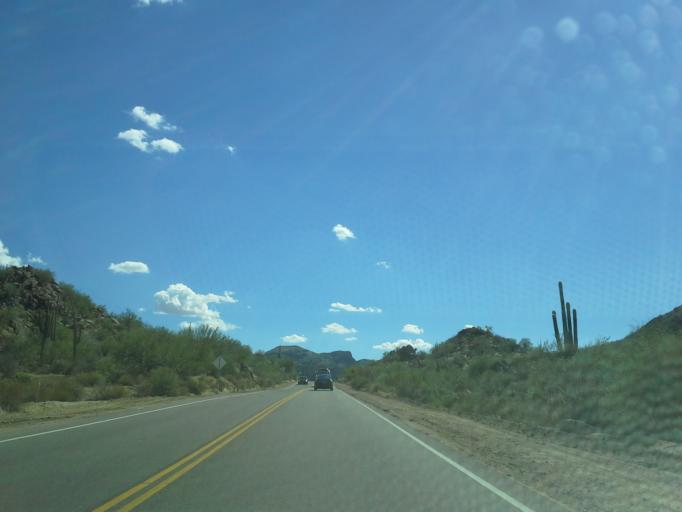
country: US
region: Arizona
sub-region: Pinal County
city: Apache Junction
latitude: 33.5700
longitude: -111.5447
